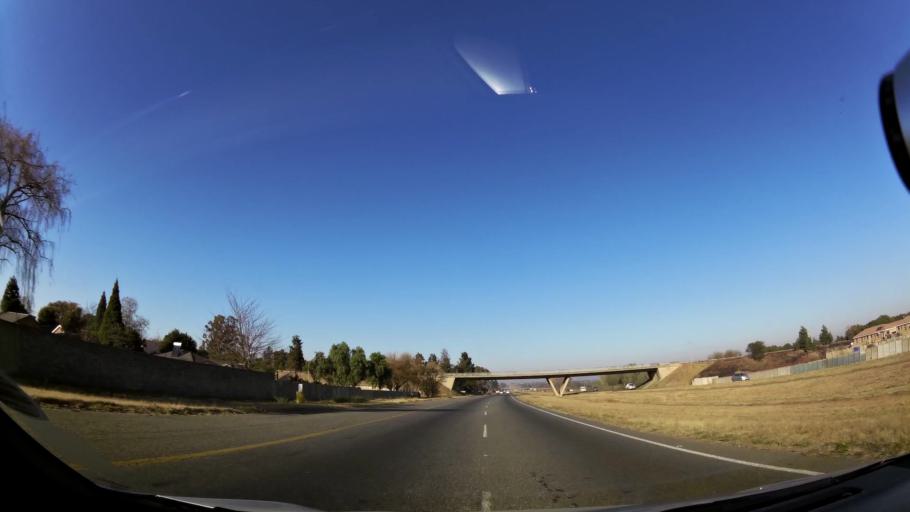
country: ZA
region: Gauteng
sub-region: Ekurhuleni Metropolitan Municipality
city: Germiston
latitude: -26.3297
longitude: 28.1116
